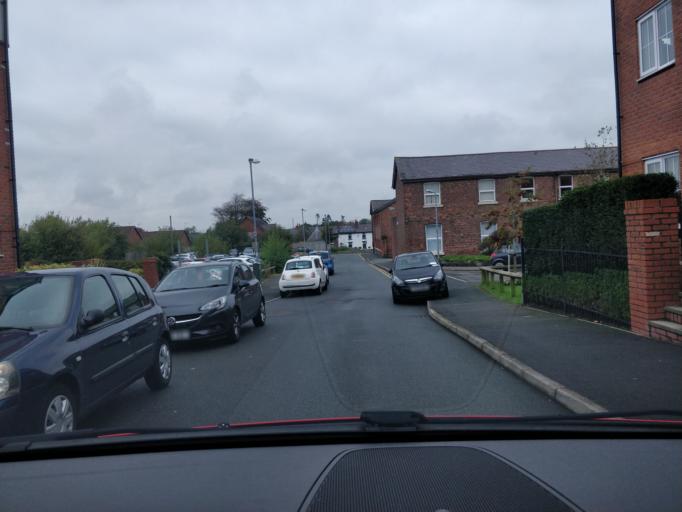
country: GB
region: England
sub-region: Lancashire
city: Ormskirk
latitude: 53.5655
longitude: -2.8767
